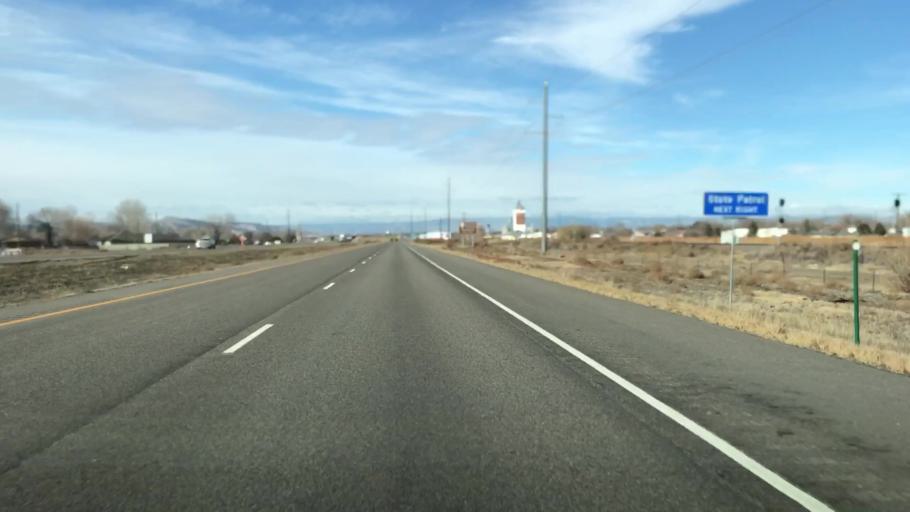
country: US
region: Colorado
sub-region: Mesa County
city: Fruita
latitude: 39.1500
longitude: -108.7249
